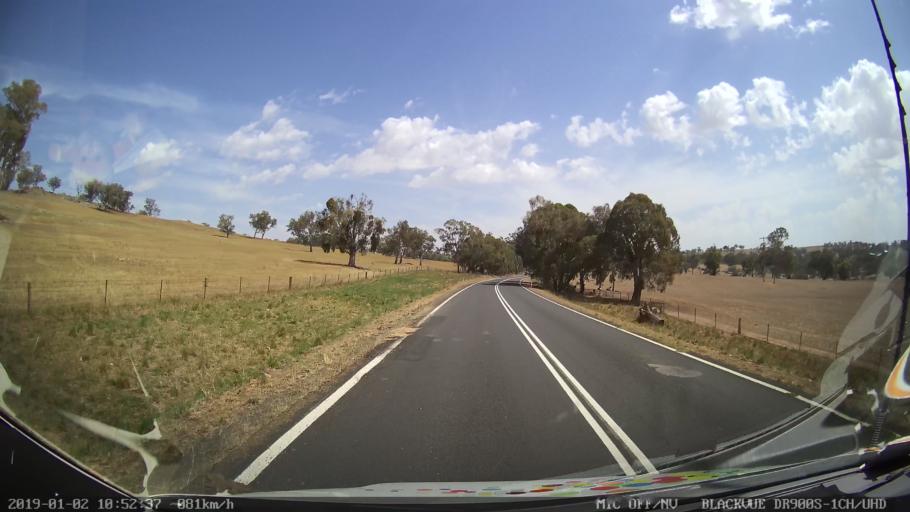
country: AU
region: New South Wales
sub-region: Cootamundra
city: Cootamundra
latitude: -34.6870
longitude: 148.2716
